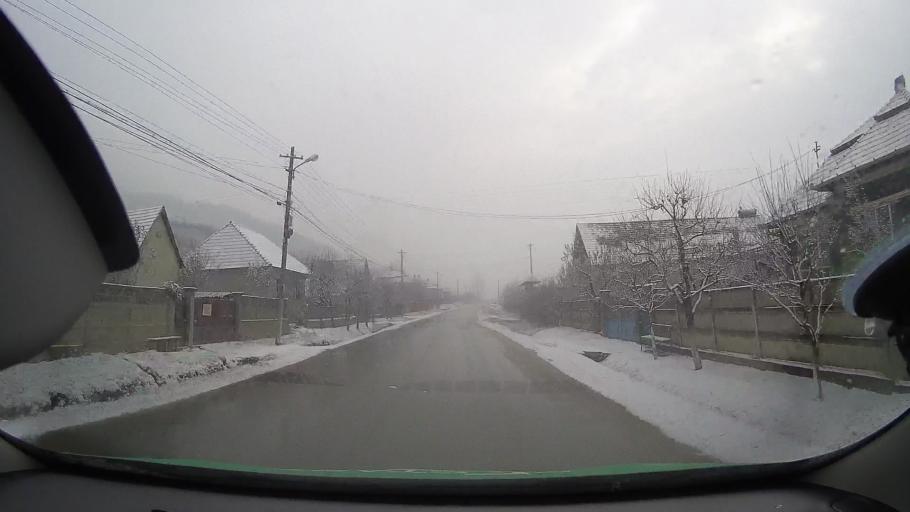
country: RO
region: Alba
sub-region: Comuna Lopadea Noua
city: Lopadea Noua
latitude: 46.3061
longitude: 23.7983
